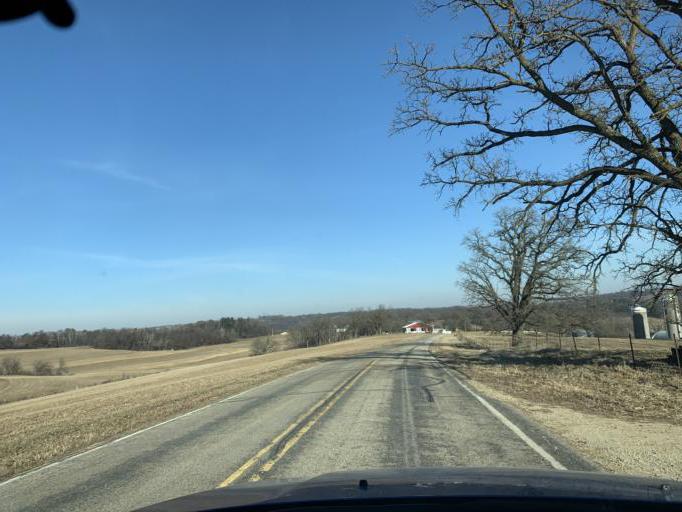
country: US
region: Wisconsin
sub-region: Iowa County
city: Barneveld
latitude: 42.8645
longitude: -89.9378
